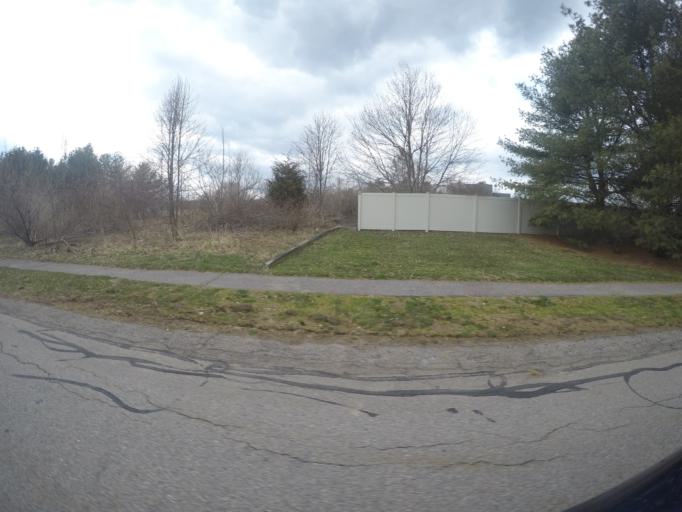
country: US
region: Massachusetts
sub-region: Bristol County
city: Easton
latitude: 42.0560
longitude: -71.1335
